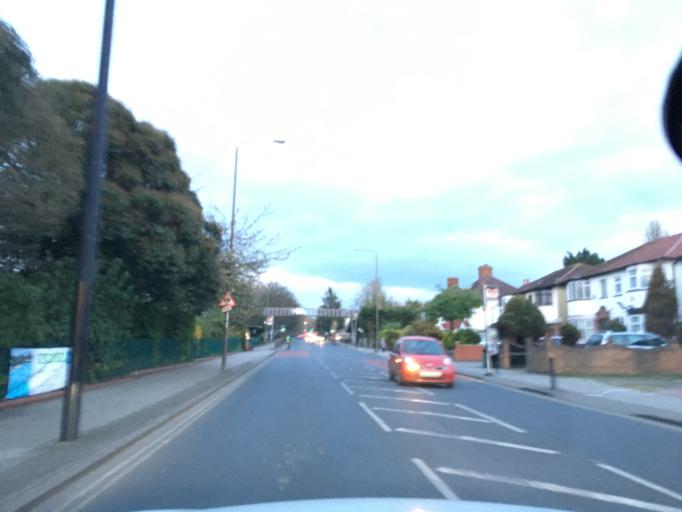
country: GB
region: England
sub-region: Greater London
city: Blackheath
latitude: 51.4743
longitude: 0.0376
